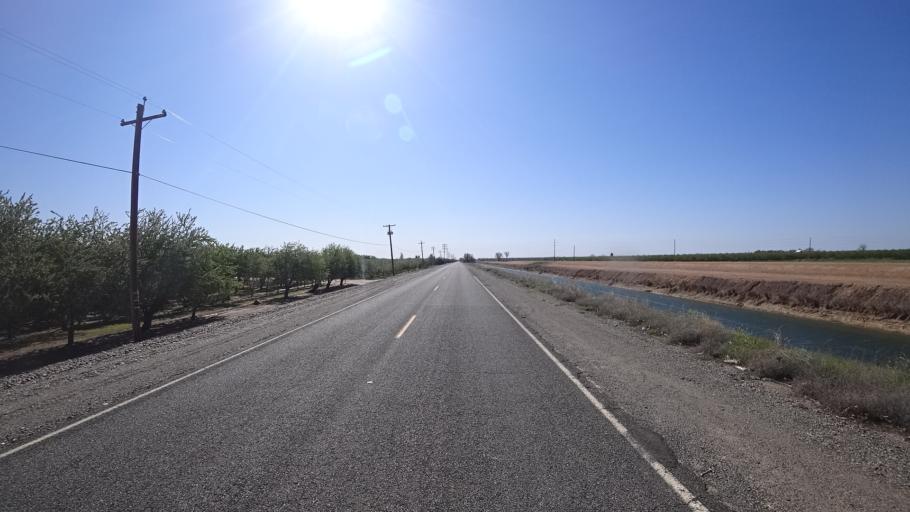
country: US
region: California
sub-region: Glenn County
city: Hamilton City
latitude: 39.7778
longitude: -122.0405
